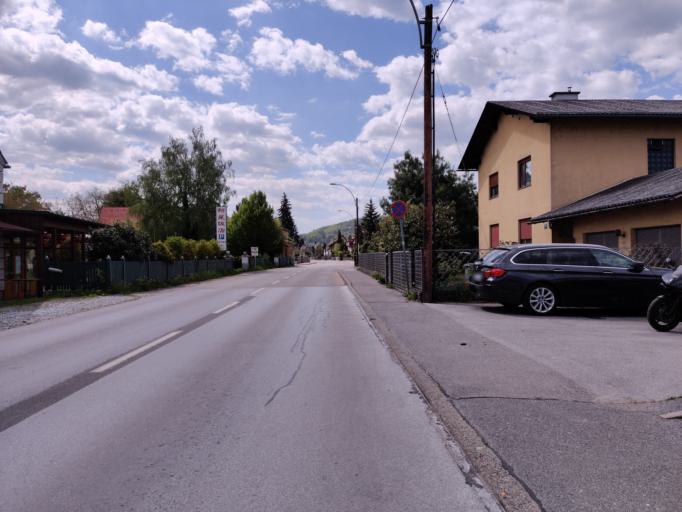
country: AT
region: Styria
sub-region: Graz Stadt
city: Wetzelsdorf
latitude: 47.0389
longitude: 15.4004
